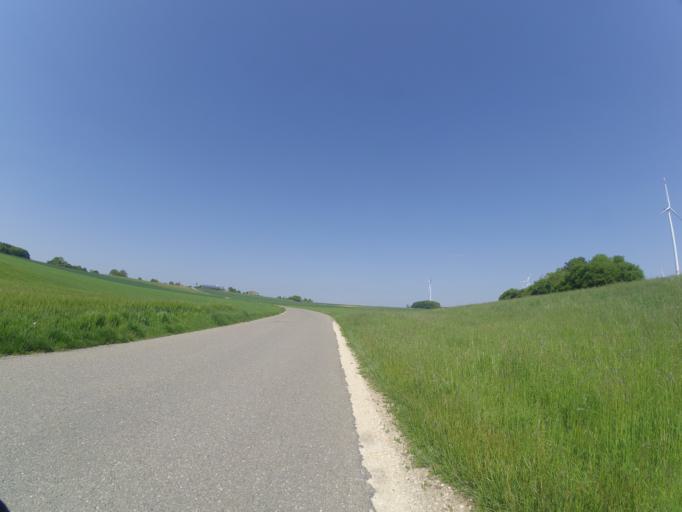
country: DE
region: Baden-Wuerttemberg
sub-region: Tuebingen Region
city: Dornstadt
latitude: 48.4615
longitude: 9.8743
